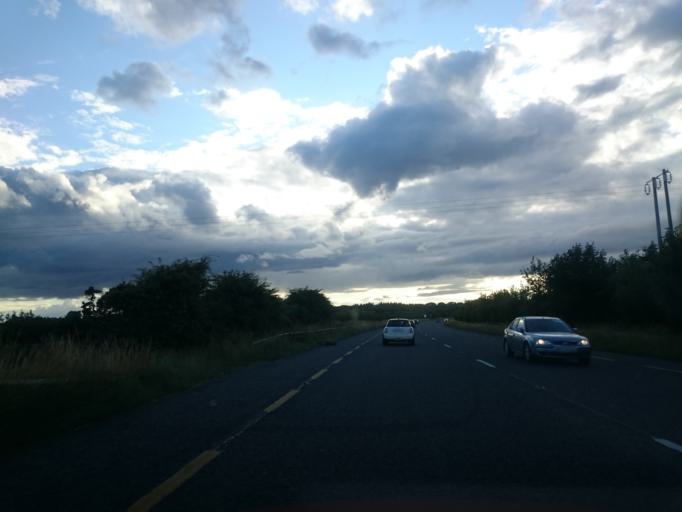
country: IE
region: Leinster
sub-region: Loch Garman
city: Loch Garman
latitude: 52.3037
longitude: -6.4691
